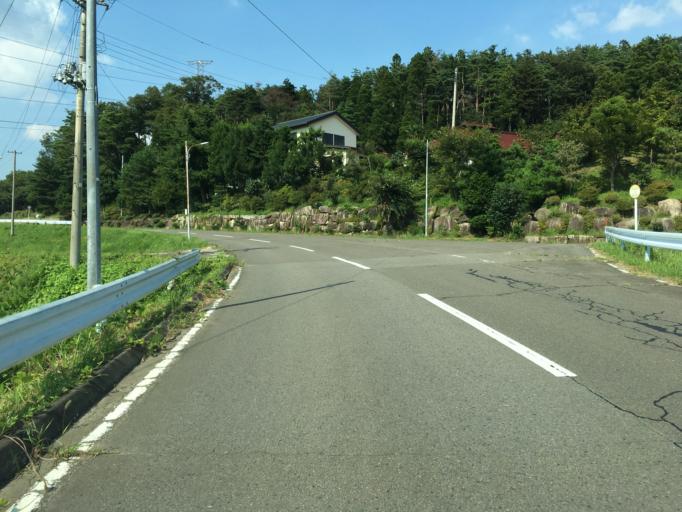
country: JP
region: Fukushima
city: Nihommatsu
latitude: 37.5768
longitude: 140.3847
